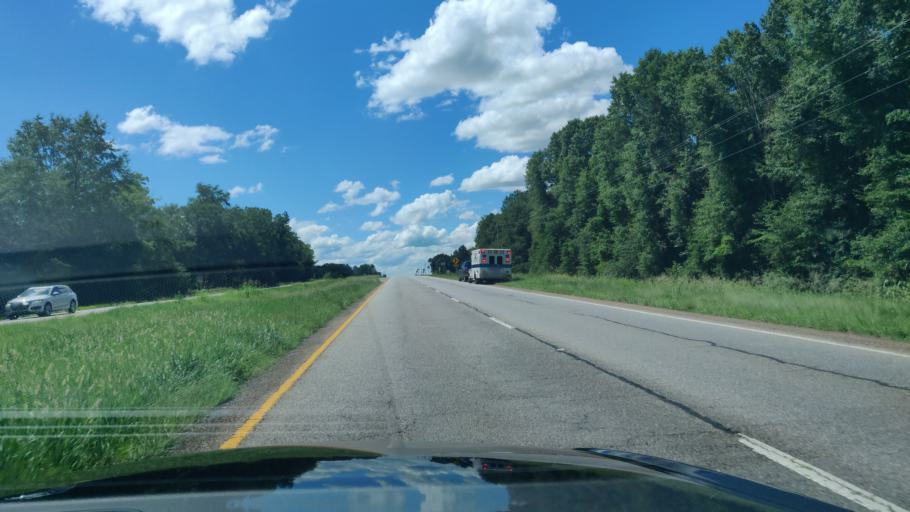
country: US
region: Georgia
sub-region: Stewart County
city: Richland
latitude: 32.0087
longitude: -84.6530
